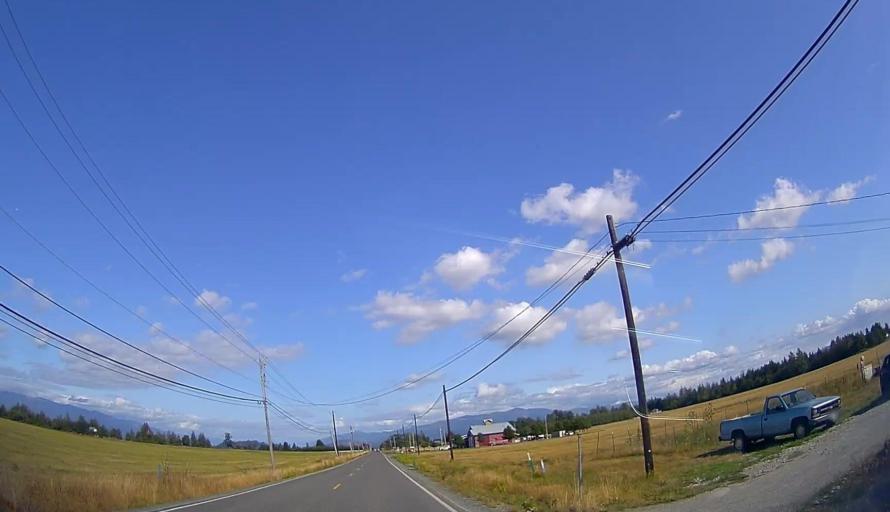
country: US
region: Washington
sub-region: Skagit County
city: Burlington
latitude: 48.4723
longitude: -122.3985
